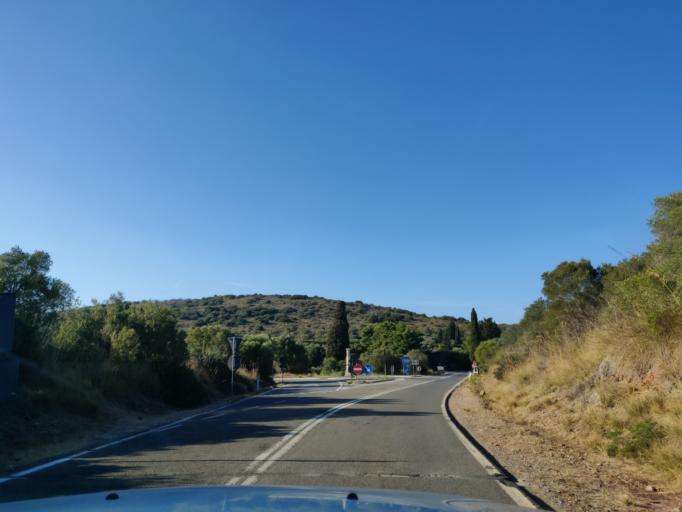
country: IT
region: Tuscany
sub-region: Provincia di Grosseto
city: Orbetello Scalo
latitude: 42.4174
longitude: 11.2987
